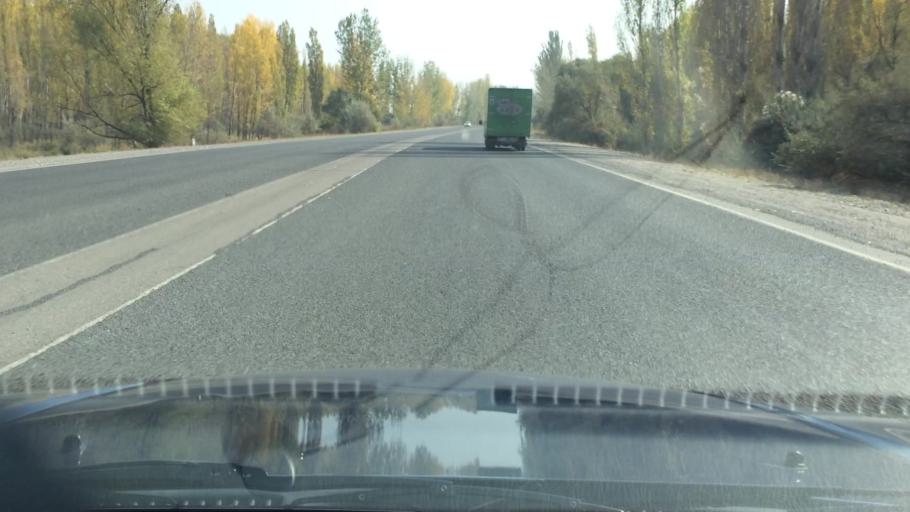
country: KG
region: Chuy
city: Ivanovka
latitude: 42.9377
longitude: 74.9859
